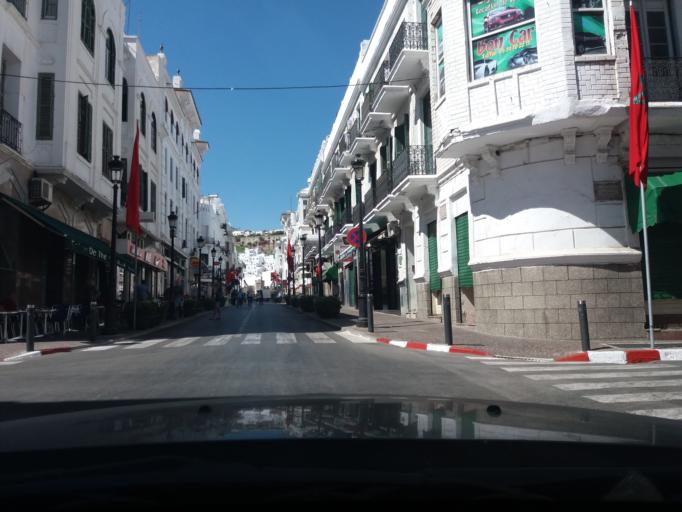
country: MA
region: Tanger-Tetouan
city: Tetouan
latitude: 35.5695
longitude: -5.3721
